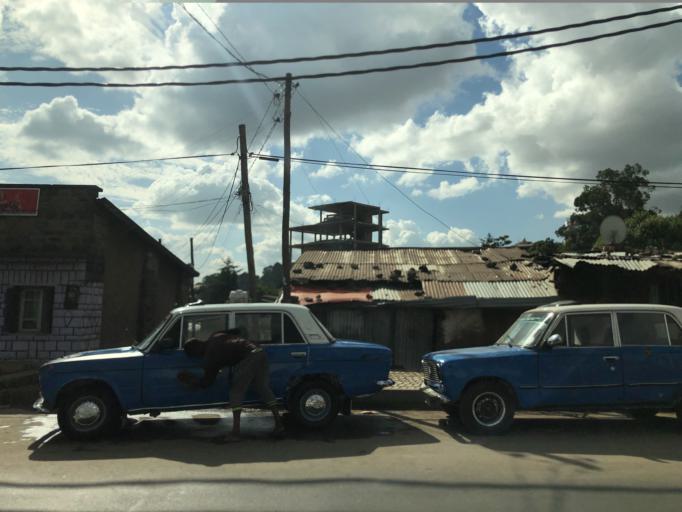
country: ET
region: Adis Abeba
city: Addis Ababa
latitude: 9.0311
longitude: 38.7737
